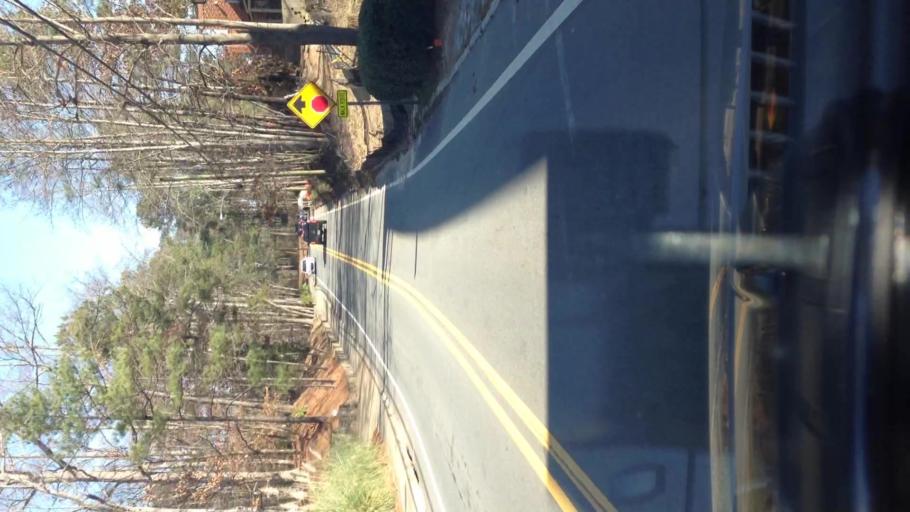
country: US
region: Georgia
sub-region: DeKalb County
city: North Atlanta
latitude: 33.8804
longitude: -84.3290
